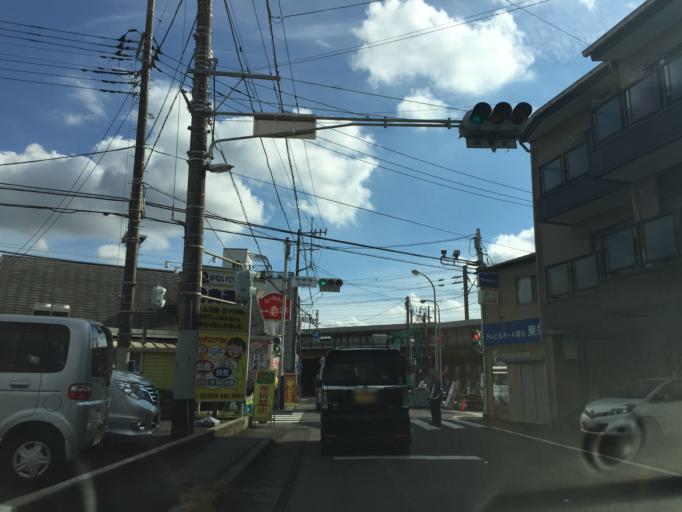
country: JP
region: Shizuoka
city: Mishima
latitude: 35.1261
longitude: 138.9017
